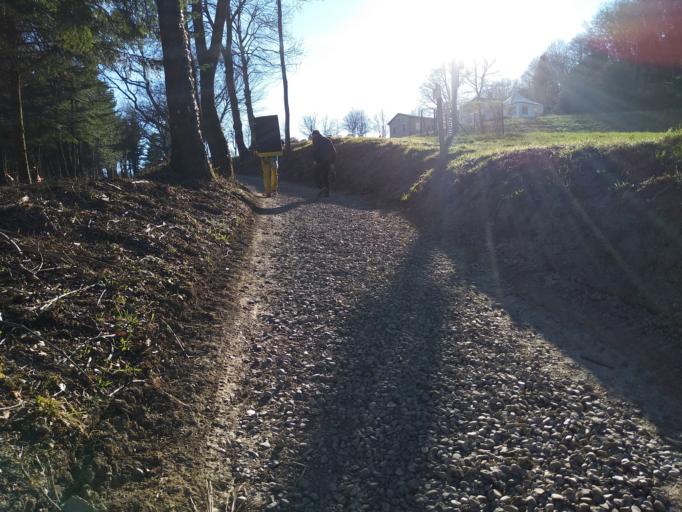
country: IT
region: Emilia-Romagna
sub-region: Provincia di Reggio Emilia
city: Castelnovo ne'Monti
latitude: 44.4182
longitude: 10.4138
